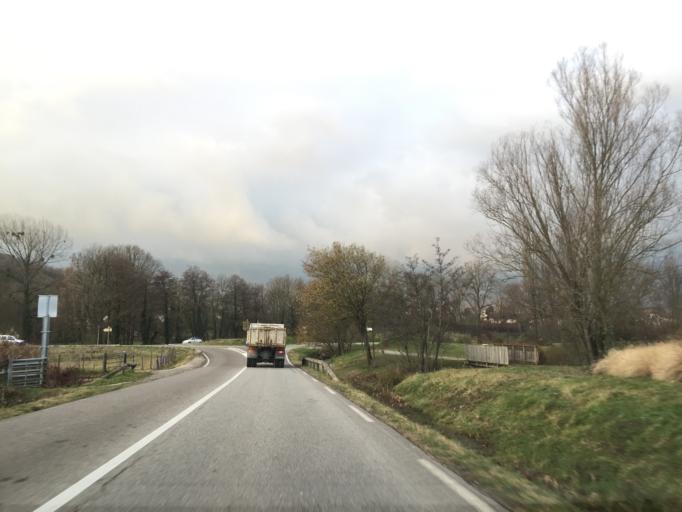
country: FR
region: Rhone-Alpes
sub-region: Departement de la Savoie
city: Voglans
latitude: 45.6429
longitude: 5.9123
